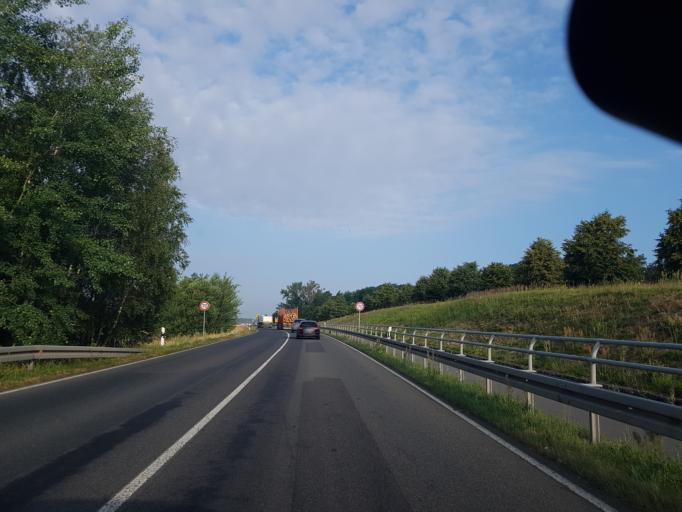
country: DE
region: Brandenburg
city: Schlieben
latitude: 51.7319
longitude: 13.3287
